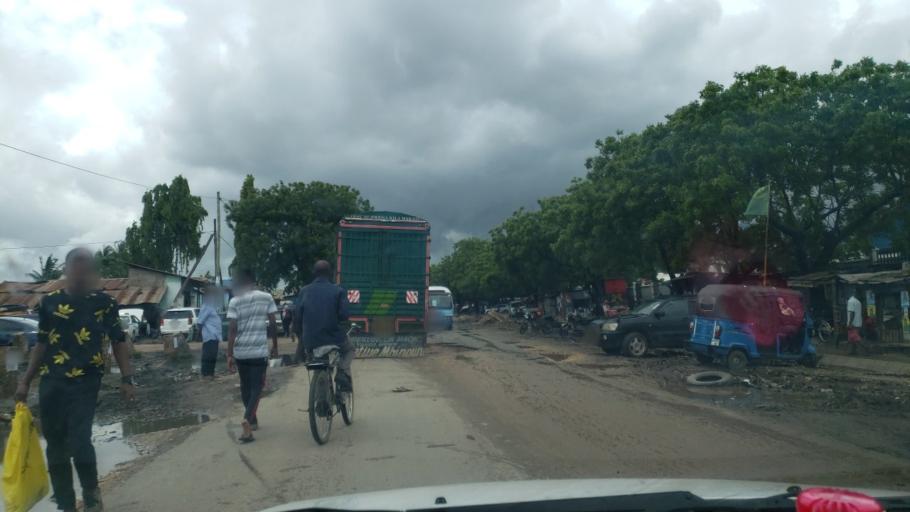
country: TZ
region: Dar es Salaam
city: Magomeni
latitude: -6.8023
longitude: 39.2248
